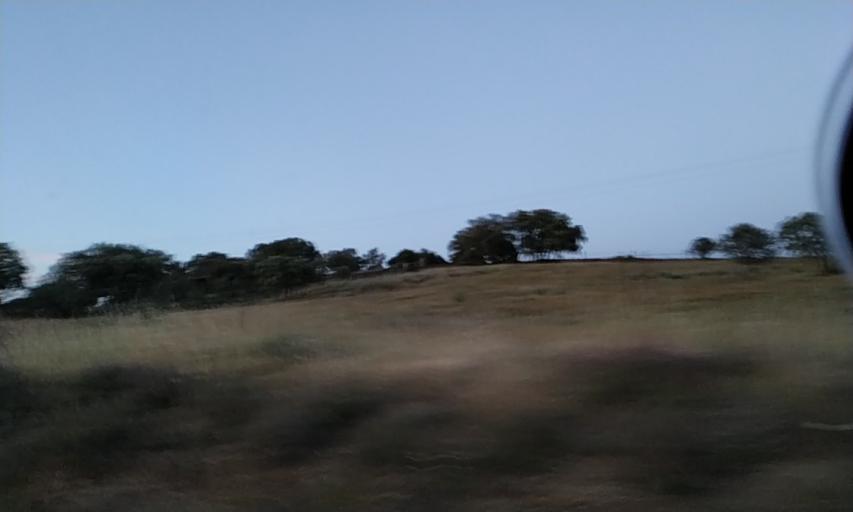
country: ES
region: Extremadura
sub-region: Provincia de Caceres
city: Piedras Albas
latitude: 39.7762
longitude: -6.9198
